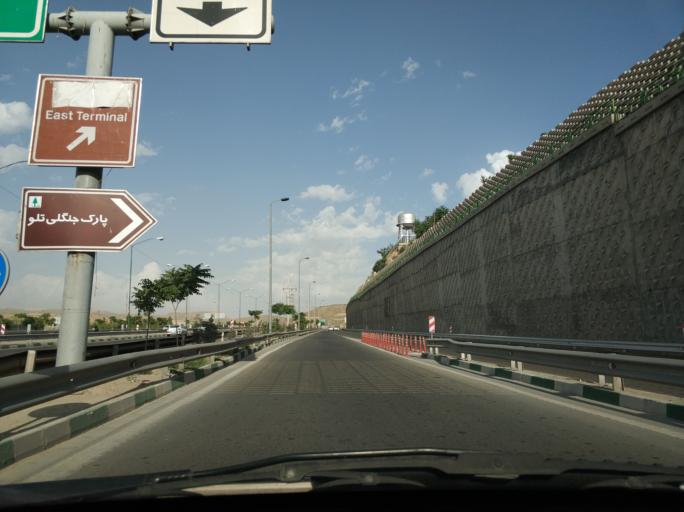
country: IR
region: Tehran
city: Tajrish
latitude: 35.7448
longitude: 51.6024
